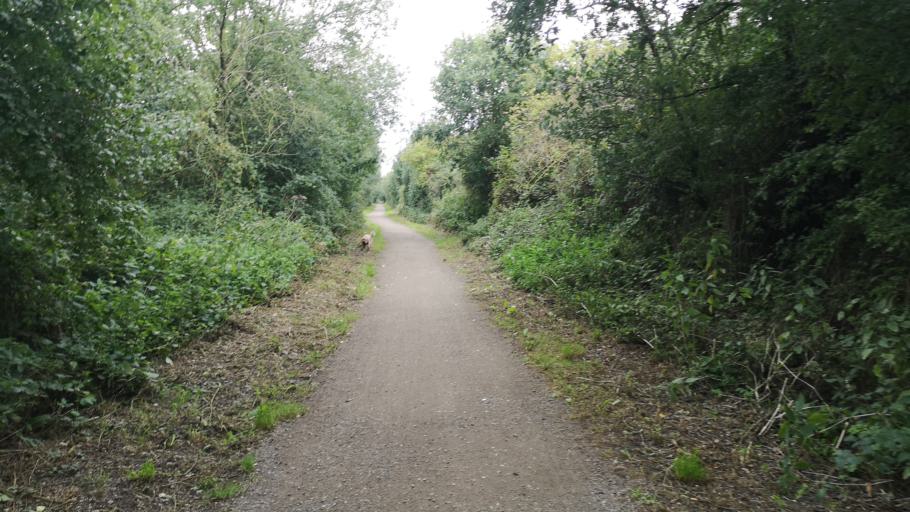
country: GB
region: England
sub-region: Barnsley
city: Royston
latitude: 53.6195
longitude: -1.4640
